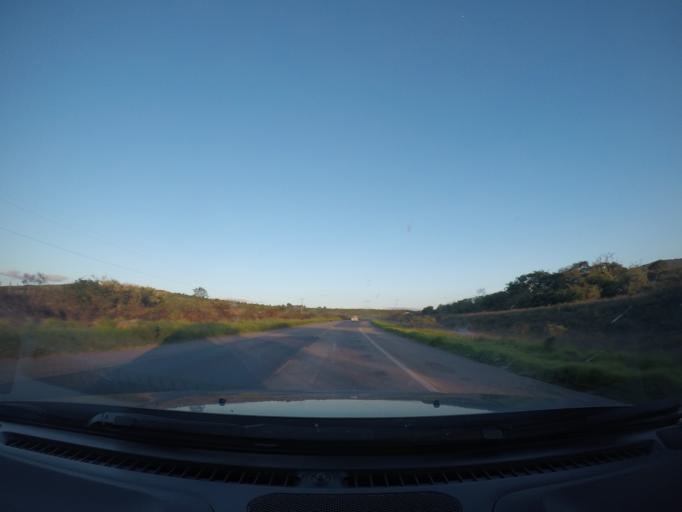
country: BR
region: Bahia
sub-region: Seabra
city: Seabra
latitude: -12.3889
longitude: -41.8900
